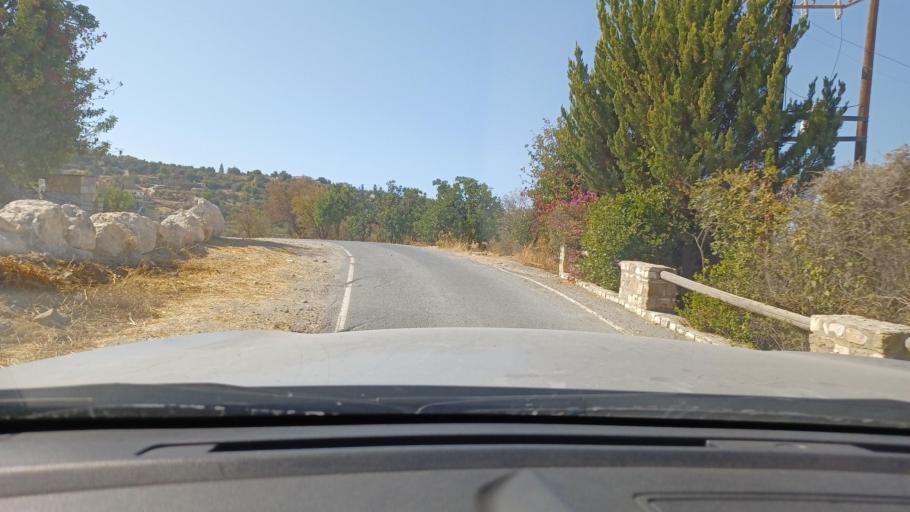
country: CY
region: Pafos
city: Polis
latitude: 34.9961
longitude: 32.4964
